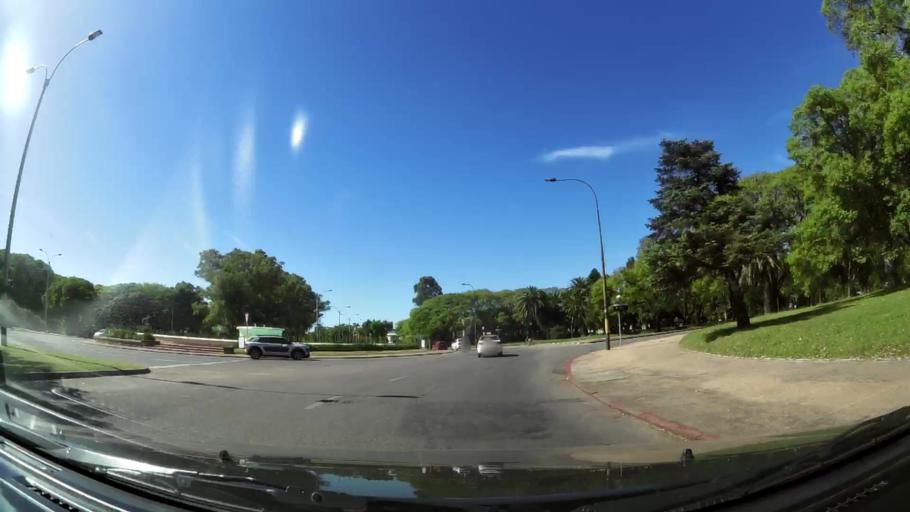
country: UY
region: Montevideo
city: Montevideo
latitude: -34.8956
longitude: -56.1596
